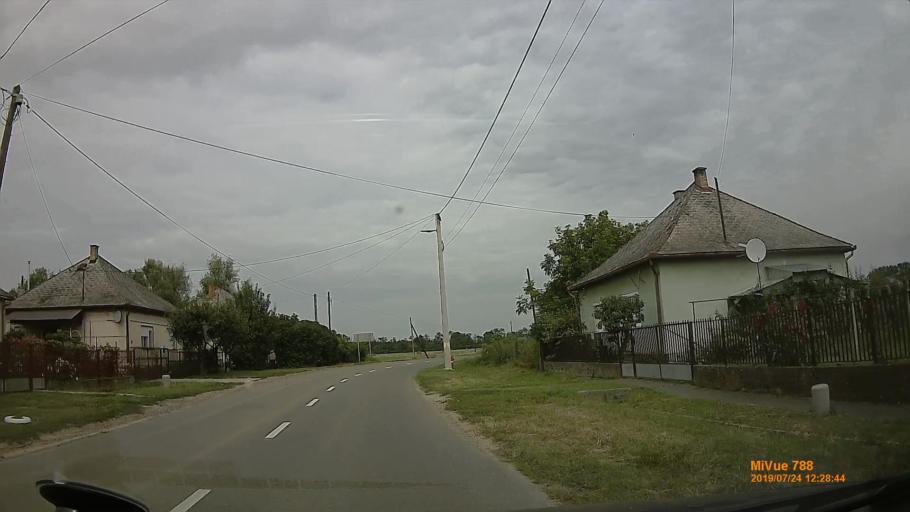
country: HU
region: Szabolcs-Szatmar-Bereg
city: Vasarosnameny
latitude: 48.1442
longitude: 22.3454
